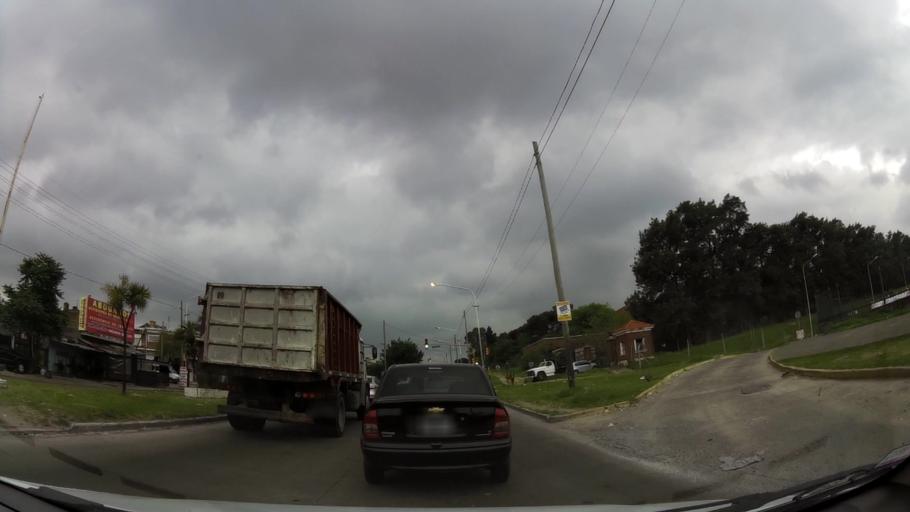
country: AR
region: Buenos Aires
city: San Justo
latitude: -34.6986
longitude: -58.5391
